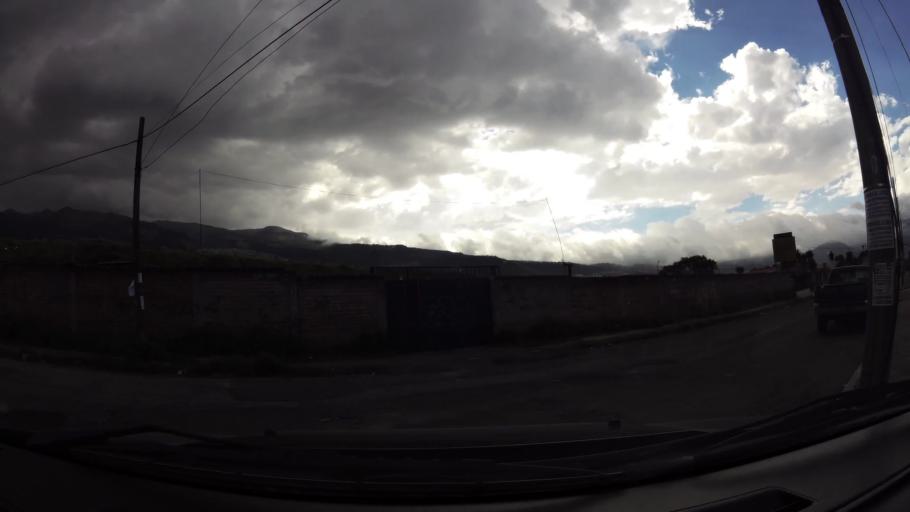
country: EC
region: Pichincha
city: Quito
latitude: -0.1253
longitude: -78.4897
